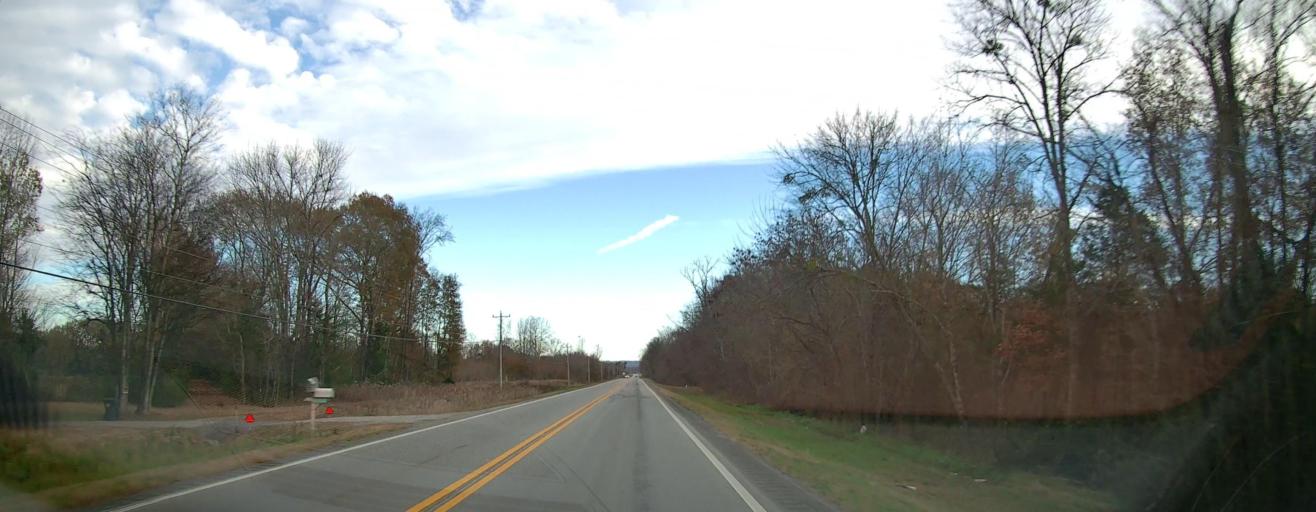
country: US
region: Alabama
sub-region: Morgan County
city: Falkville
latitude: 34.4235
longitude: -86.7181
